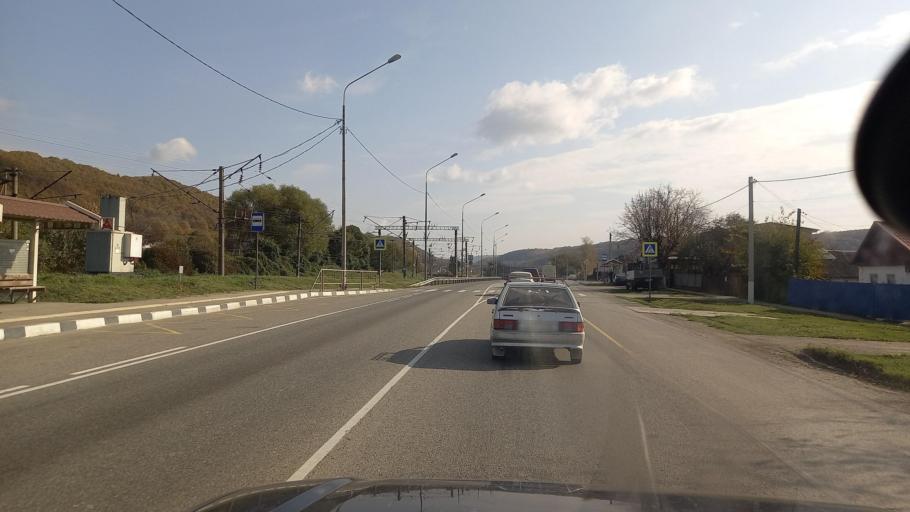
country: RU
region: Krasnodarskiy
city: Krymsk
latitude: 44.8685
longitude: 37.8704
